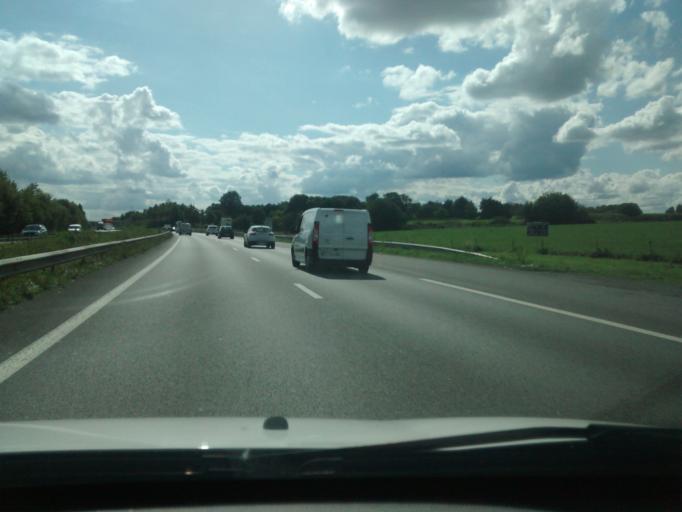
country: FR
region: Brittany
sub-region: Departement d'Ille-et-Vilaine
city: Saint-Gregoire
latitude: 48.1368
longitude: -1.7036
